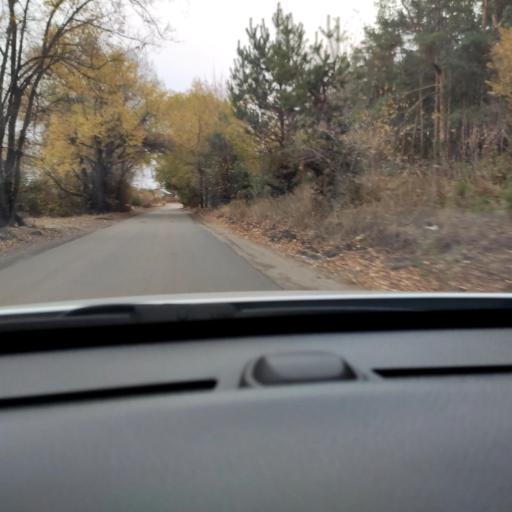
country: RU
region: Voronezj
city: Maslovka
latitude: 51.6021
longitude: 39.2739
